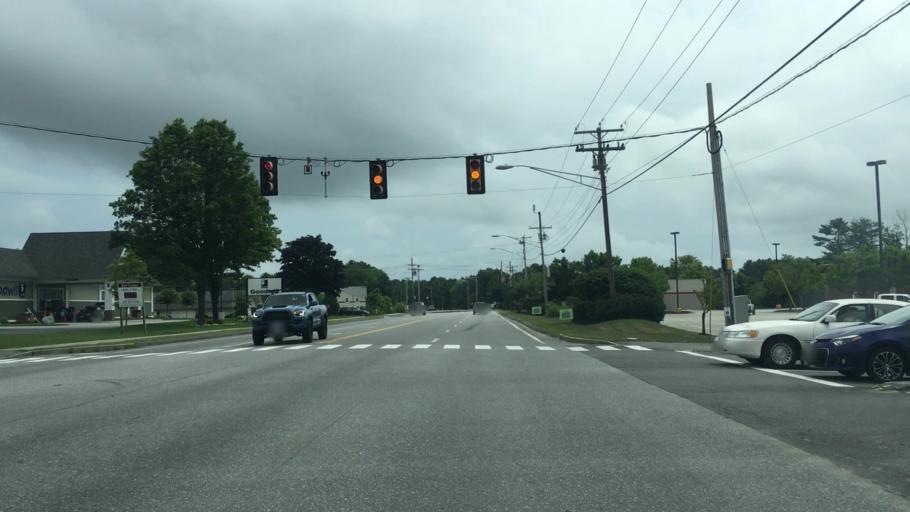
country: US
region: Maine
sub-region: Cumberland County
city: Brunswick
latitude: 43.9052
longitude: -69.9150
